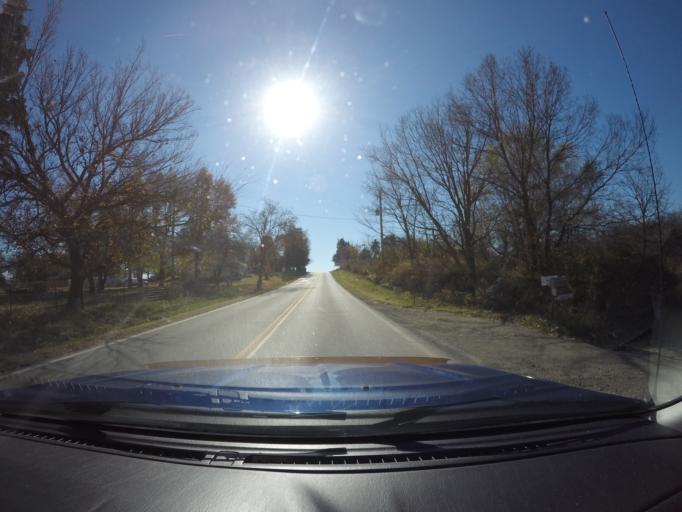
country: US
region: Kansas
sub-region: Marshall County
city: Marysville
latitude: 39.8576
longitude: -96.4171
